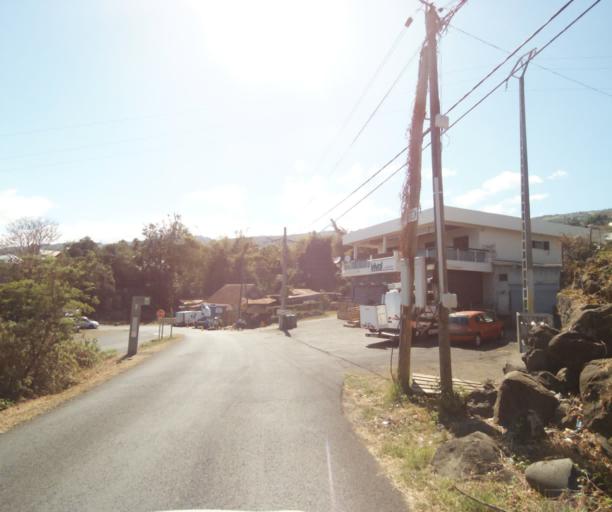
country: RE
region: Reunion
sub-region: Reunion
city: Saint-Paul
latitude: -20.9923
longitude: 55.3267
